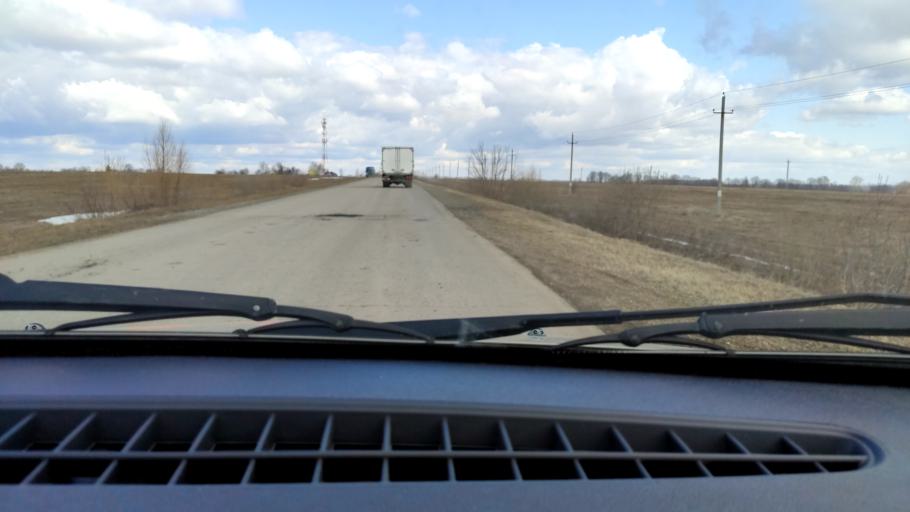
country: RU
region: Bashkortostan
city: Kudeyevskiy
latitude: 54.8367
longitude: 56.7935
